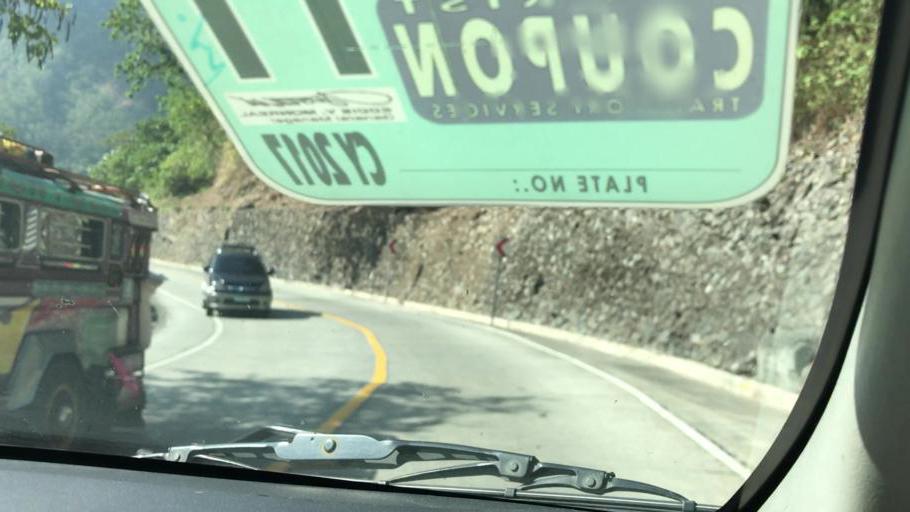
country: PH
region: Cordillera
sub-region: Province of Benguet
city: Tuba
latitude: 16.3170
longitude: 120.6183
